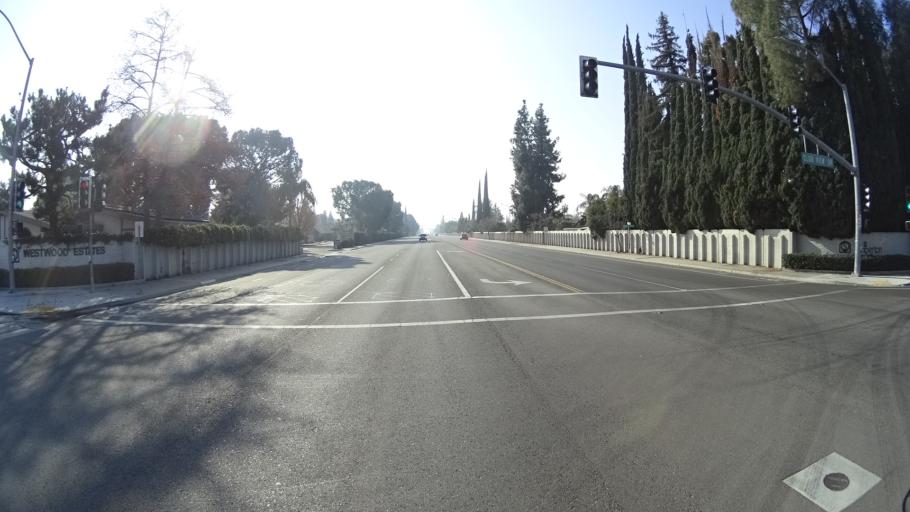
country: US
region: California
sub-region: Kern County
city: Greenacres
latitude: 35.3398
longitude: -119.0744
